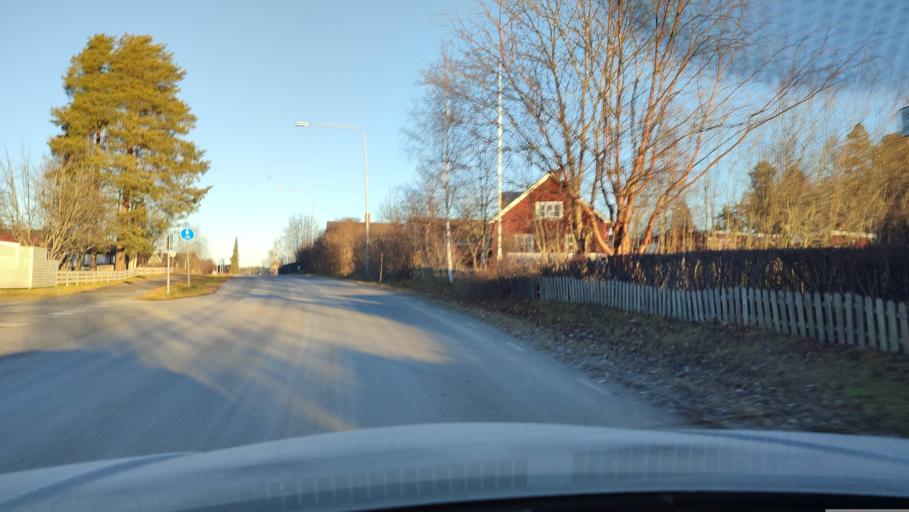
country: SE
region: Vaesterbotten
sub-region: Skelleftea Kommun
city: Viken
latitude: 64.7436
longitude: 20.9200
